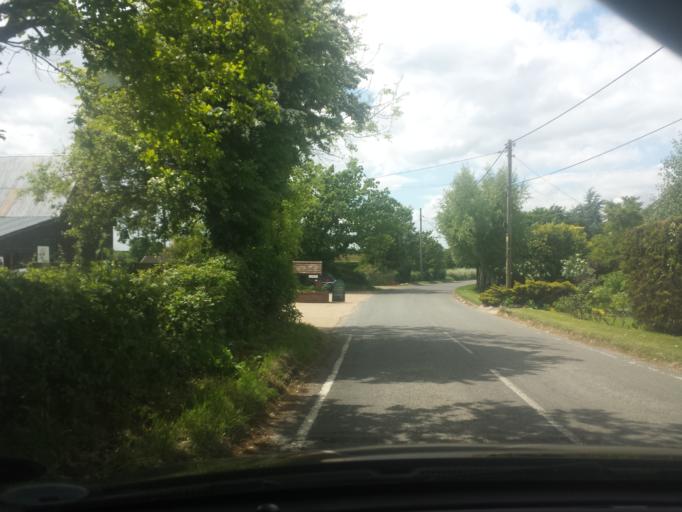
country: GB
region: England
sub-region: Essex
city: Little Clacton
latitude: 51.8816
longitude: 1.1592
